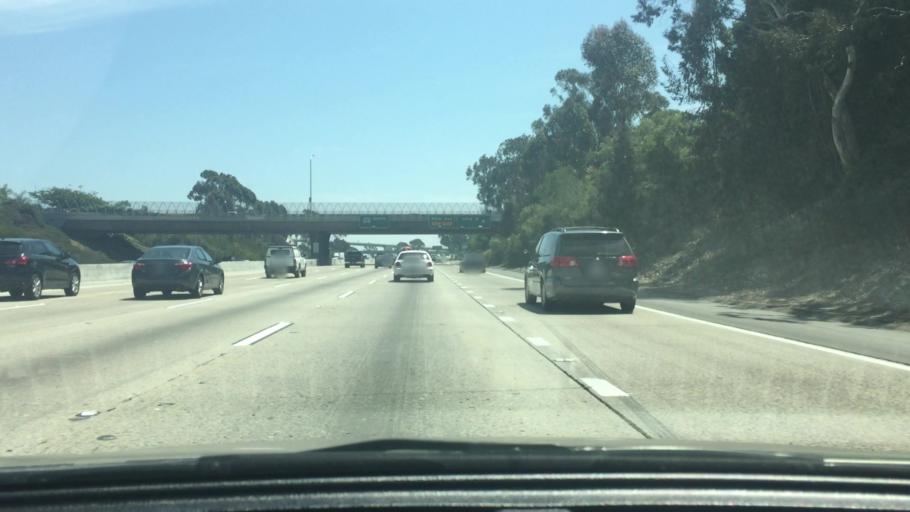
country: US
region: California
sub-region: San Diego County
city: National City
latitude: 32.6982
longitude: -117.0951
